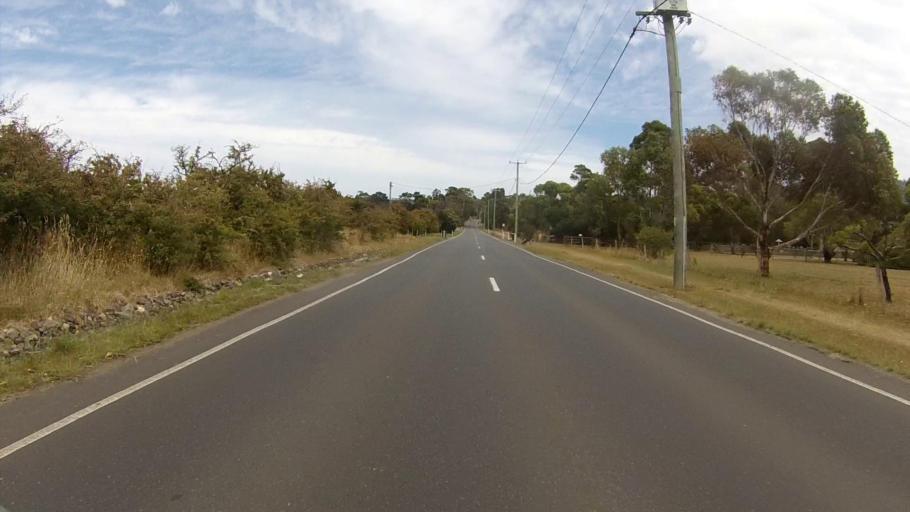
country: AU
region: Tasmania
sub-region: Clarence
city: Seven Mile Beach
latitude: -42.8641
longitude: 147.4906
